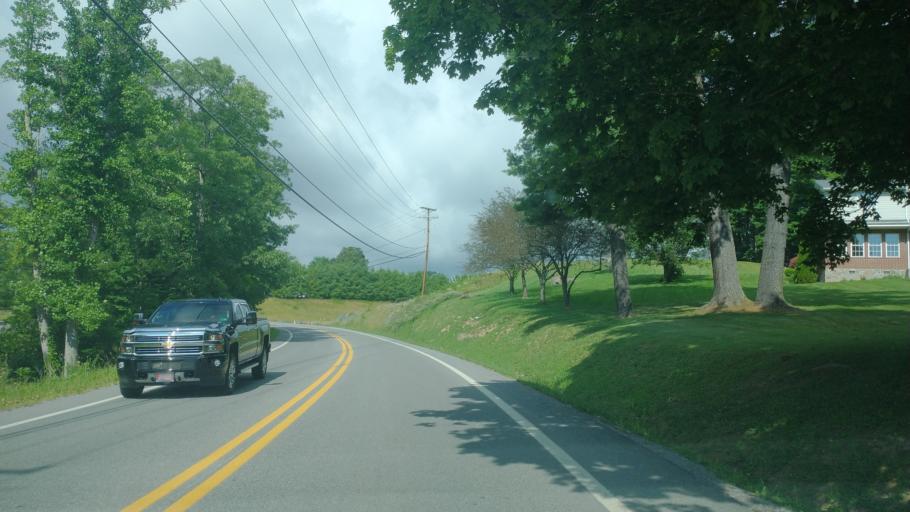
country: US
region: West Virginia
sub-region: Mercer County
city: Princeton
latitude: 37.3578
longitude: -81.1435
